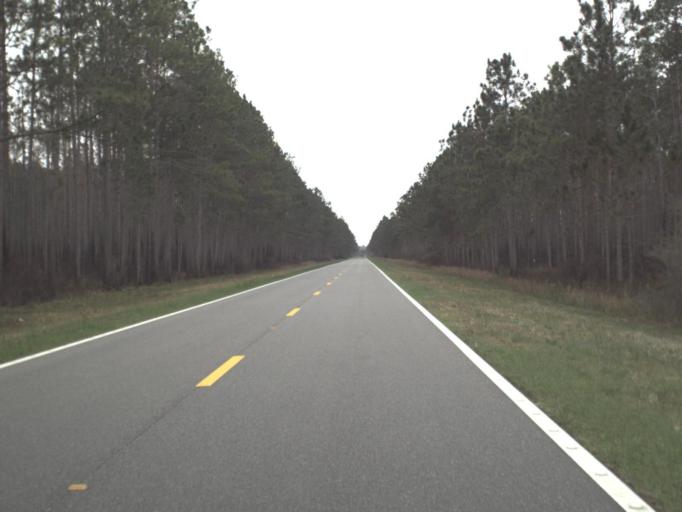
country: US
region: Florida
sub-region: Gulf County
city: Wewahitchka
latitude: 30.0507
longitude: -84.9835
